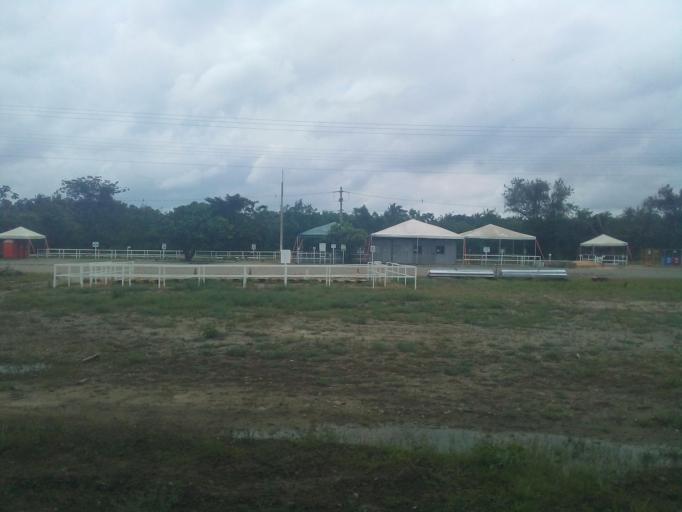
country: BR
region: Maranhao
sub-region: Santa Ines
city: Santa Ines
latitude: -3.6981
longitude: -45.4123
